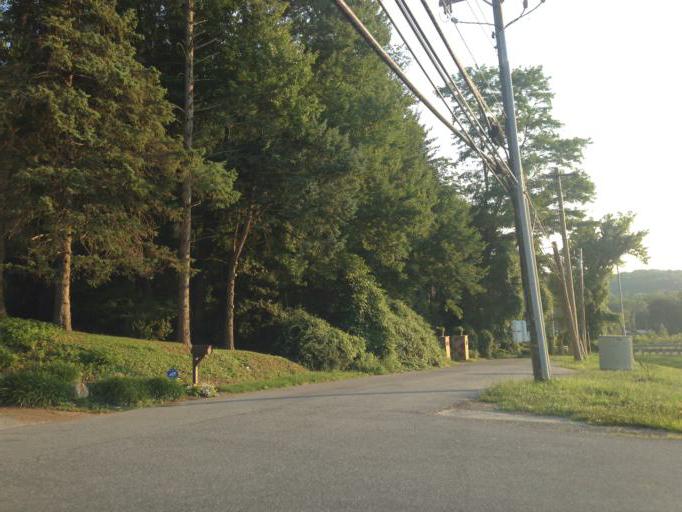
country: US
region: Maryland
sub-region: Baltimore County
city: Mays Chapel
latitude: 39.4008
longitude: -76.6611
